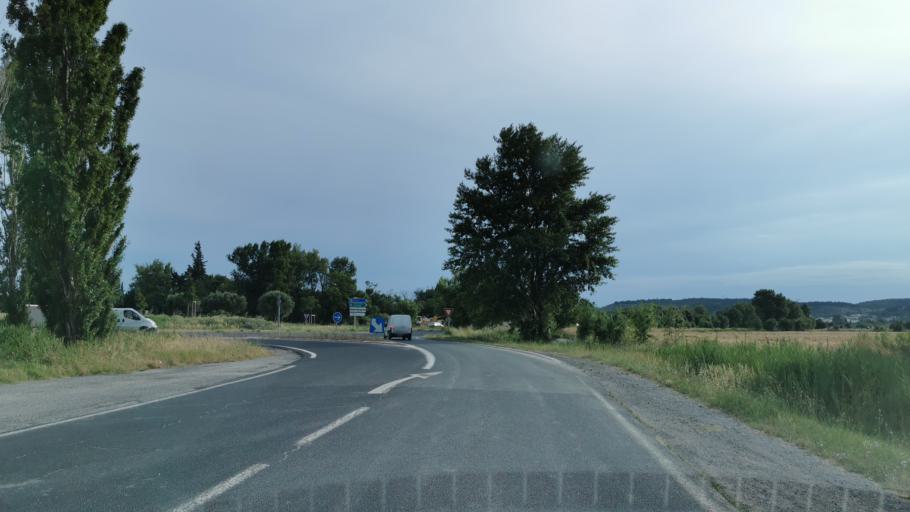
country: FR
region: Languedoc-Roussillon
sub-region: Departement de l'Aude
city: Narbonne
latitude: 43.1950
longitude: 2.9939
